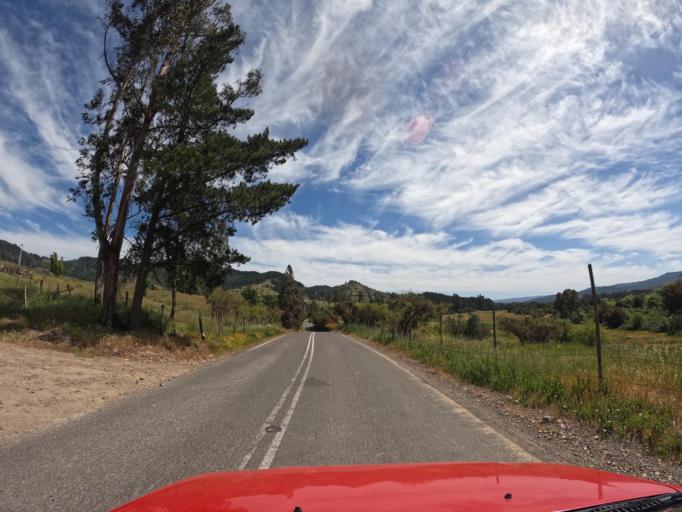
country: CL
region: Maule
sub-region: Provincia de Talca
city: Talca
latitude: -34.9912
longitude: -71.8576
